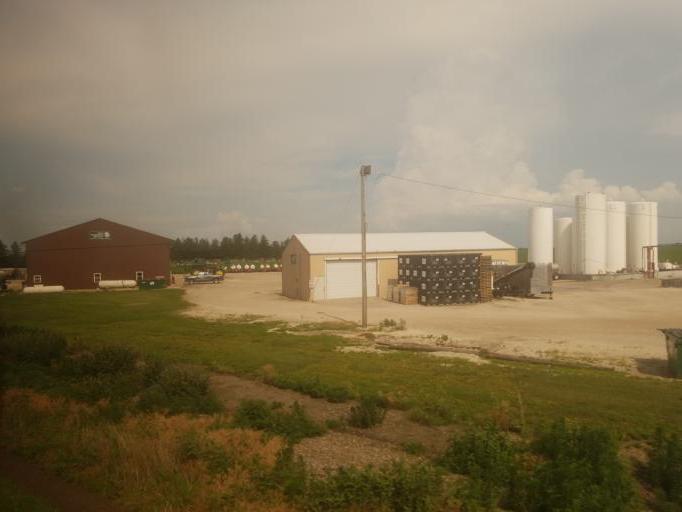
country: US
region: Illinois
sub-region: Knox County
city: Knoxville
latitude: 41.0791
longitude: -90.2167
